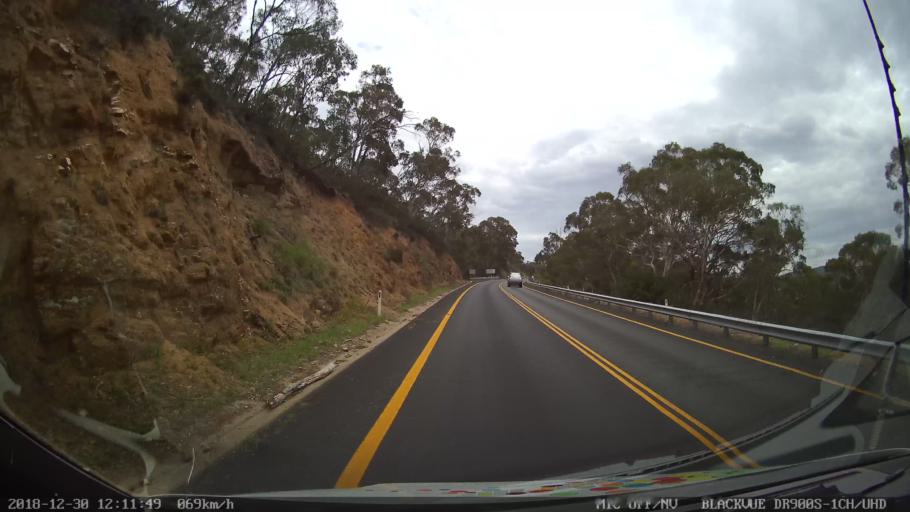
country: AU
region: New South Wales
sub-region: Snowy River
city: Jindabyne
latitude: -36.3630
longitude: 148.5869
